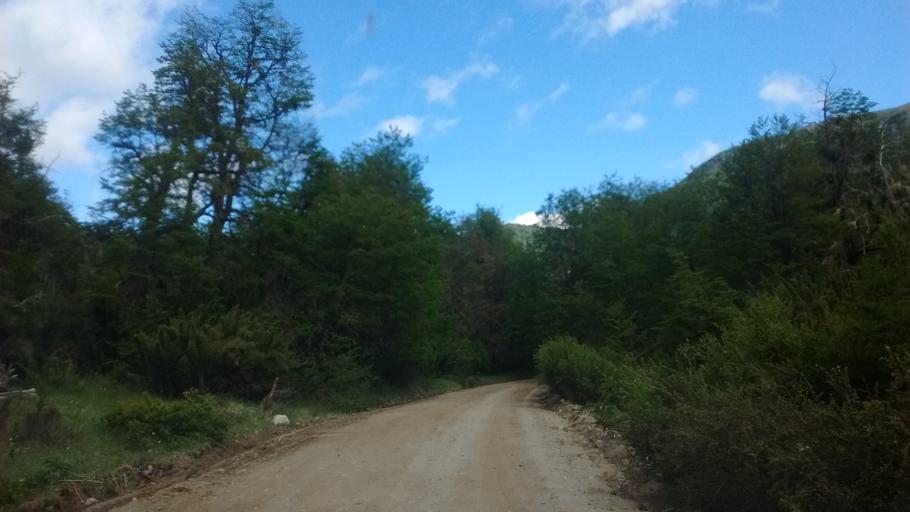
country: AR
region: Neuquen
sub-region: Departamento de Lacar
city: San Martin de los Andes
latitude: -40.3655
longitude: -71.4762
